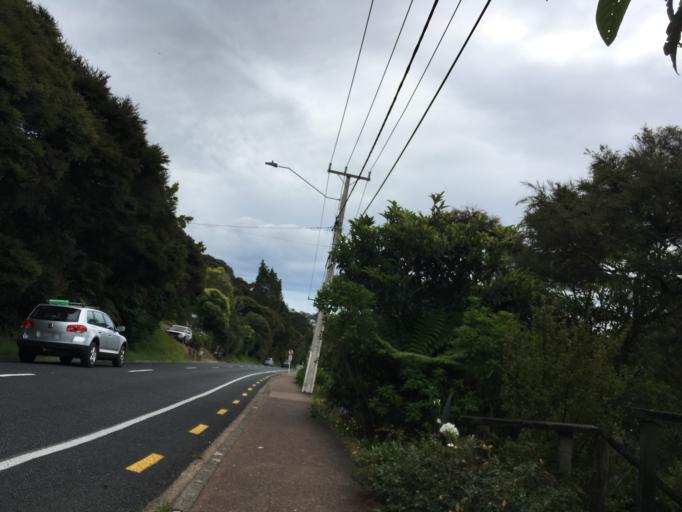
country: NZ
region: Auckland
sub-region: Auckland
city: Pakuranga
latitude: -36.7864
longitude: 175.0210
